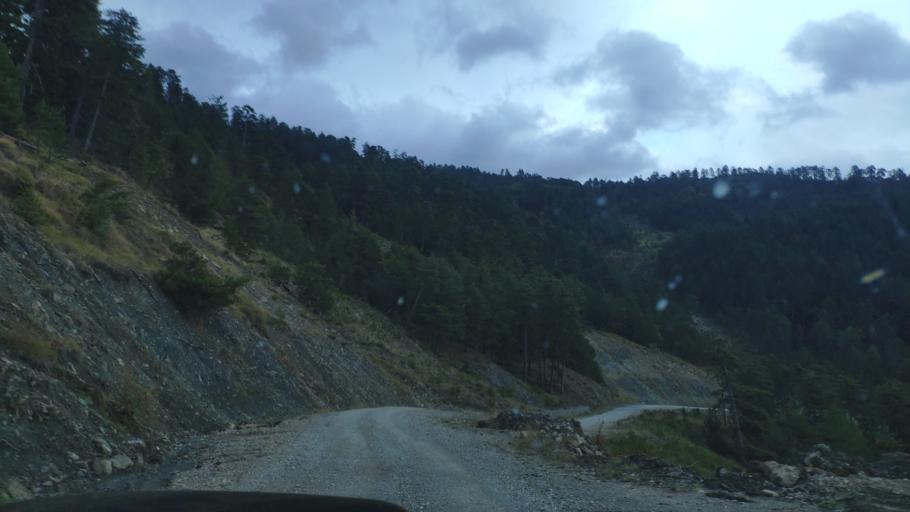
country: AL
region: Korce
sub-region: Rrethi i Kolonjes
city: Erseke
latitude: 40.2888
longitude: 20.8608
